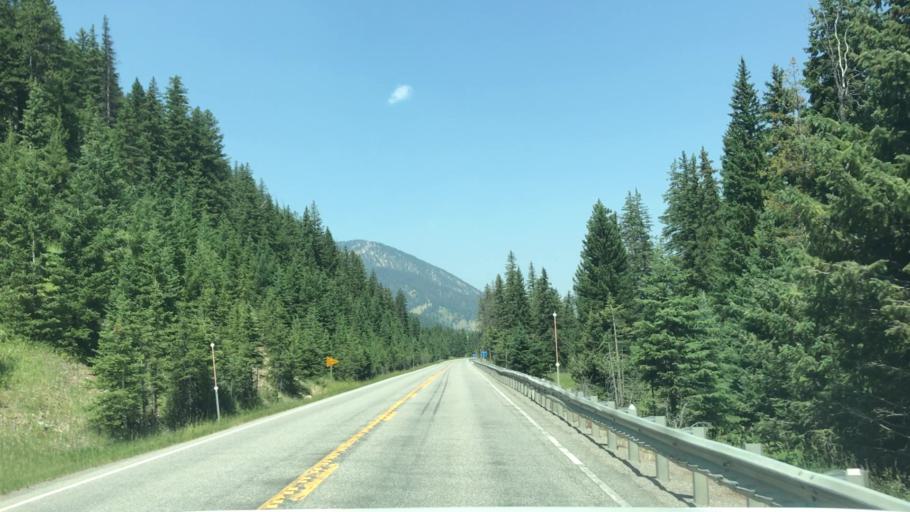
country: US
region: Montana
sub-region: Gallatin County
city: Big Sky
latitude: 45.0856
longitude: -111.2104
